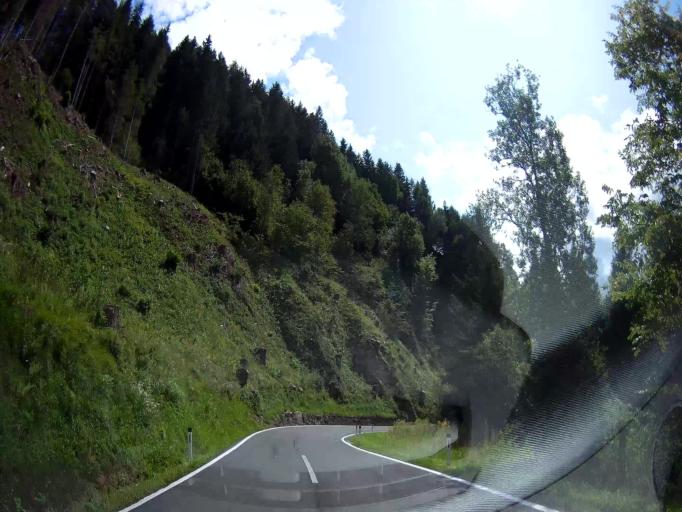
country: AT
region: Carinthia
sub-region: Politischer Bezirk Spittal an der Drau
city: Seeboden
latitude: 46.8445
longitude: 13.5012
